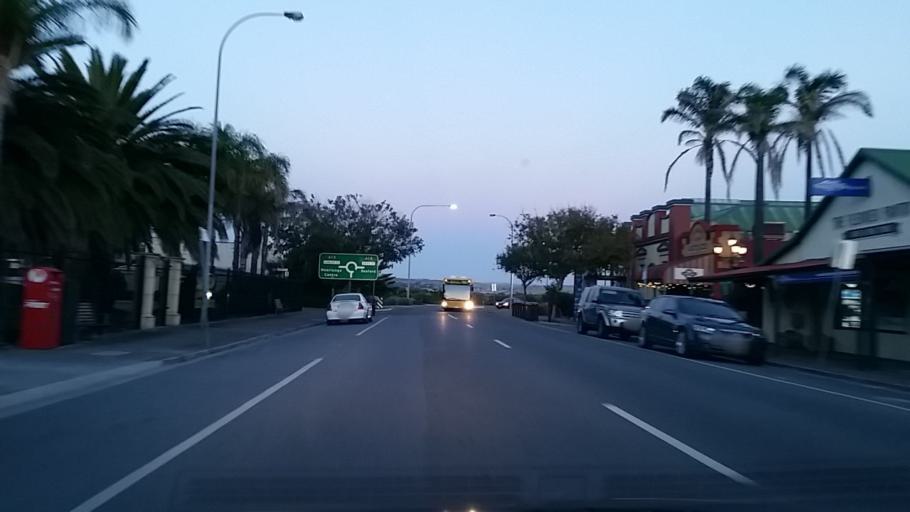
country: AU
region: South Australia
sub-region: Adelaide
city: Port Noarlunga
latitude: -35.1486
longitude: 138.4719
